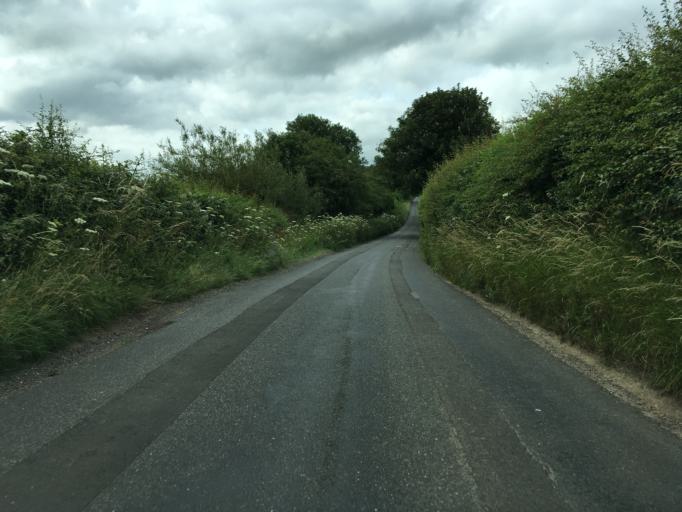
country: GB
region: England
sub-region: Oxfordshire
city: Shipton under Wychwood
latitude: 51.8760
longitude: -1.6644
